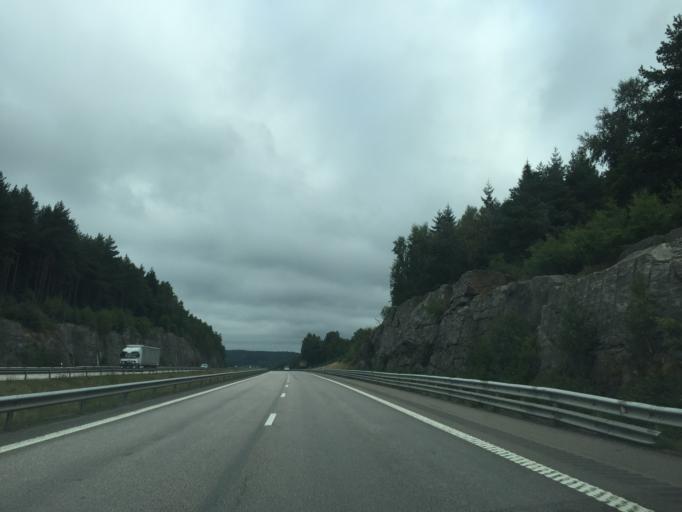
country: SE
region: Halland
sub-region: Kungsbacka Kommun
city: Frillesas
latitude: 57.3532
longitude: 12.2100
